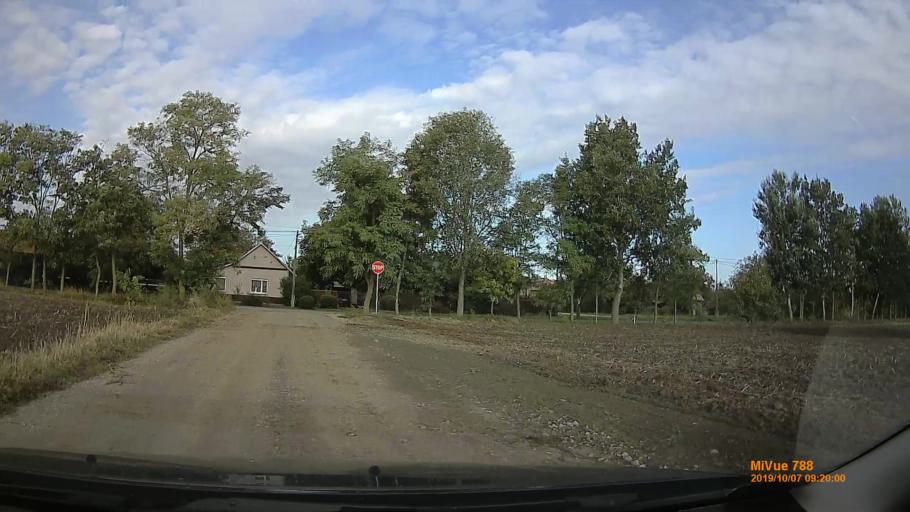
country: HU
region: Bekes
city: Szarvas
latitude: 46.8189
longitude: 20.6569
